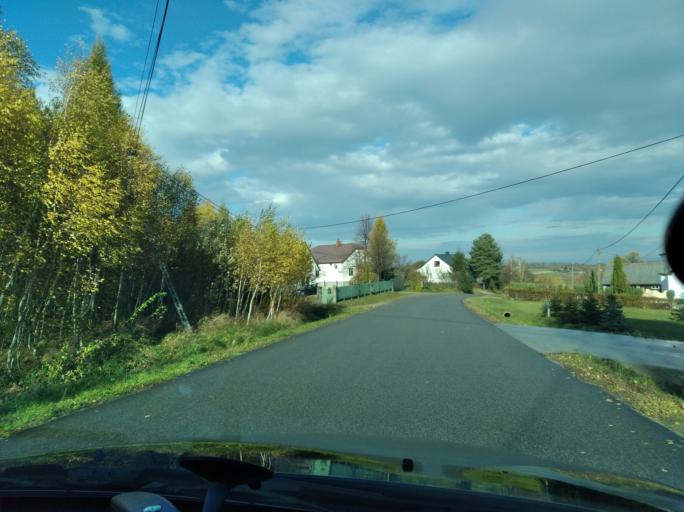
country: PL
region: Subcarpathian Voivodeship
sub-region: Powiat ropczycko-sedziszowski
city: Niedzwiada
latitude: 50.0160
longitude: 21.4768
